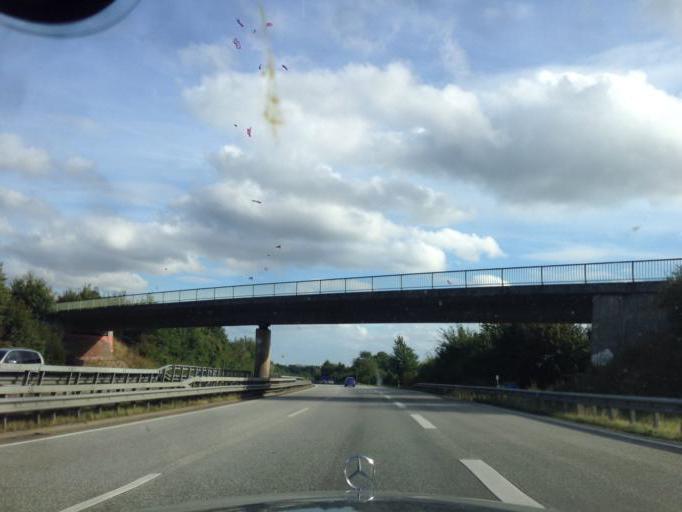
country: DE
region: Schleswig-Holstein
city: Schackendorf
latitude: 53.9576
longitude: 10.2639
